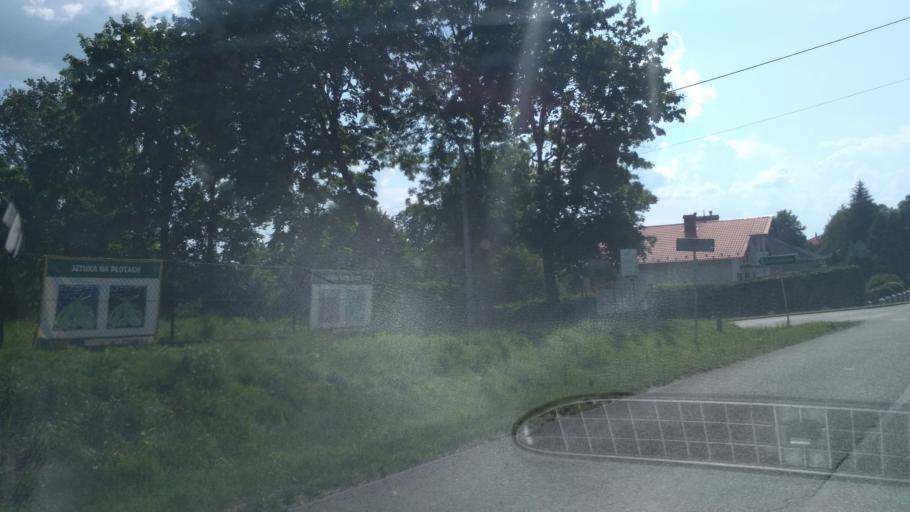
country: PL
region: Subcarpathian Voivodeship
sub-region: Powiat jaroslawski
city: Ostrow
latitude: 49.9403
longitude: 22.7399
